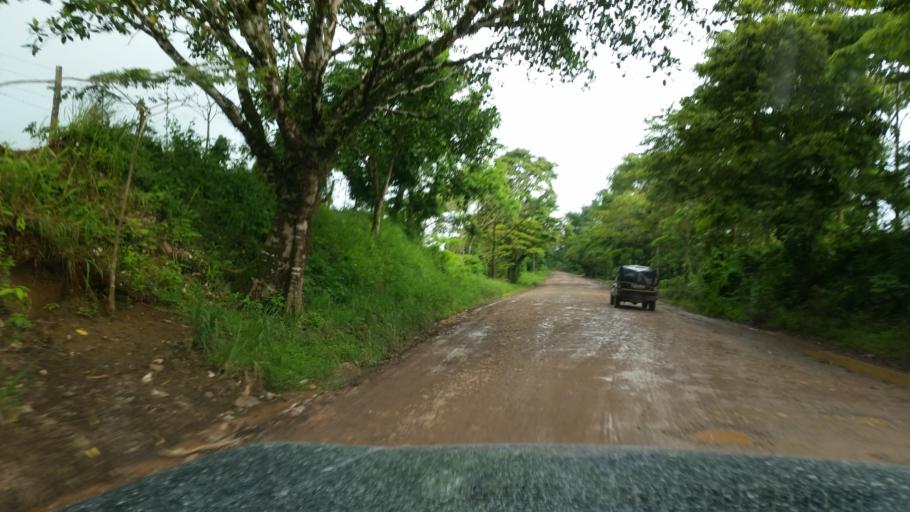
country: NI
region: Atlantico Norte (RAAN)
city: Siuna
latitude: 13.4156
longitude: -84.8534
